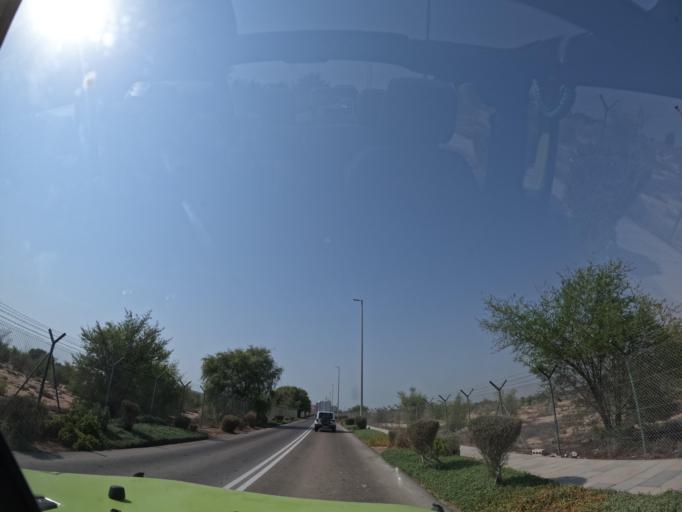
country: AE
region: Abu Dhabi
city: Abu Dhabi
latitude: 24.4760
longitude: 54.6276
